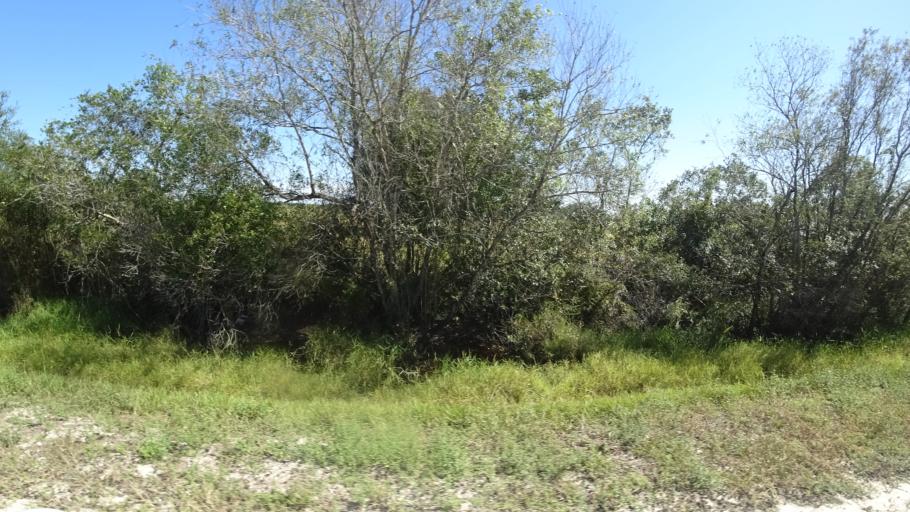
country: US
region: Florida
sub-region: DeSoto County
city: Arcadia
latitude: 27.3164
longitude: -82.0805
